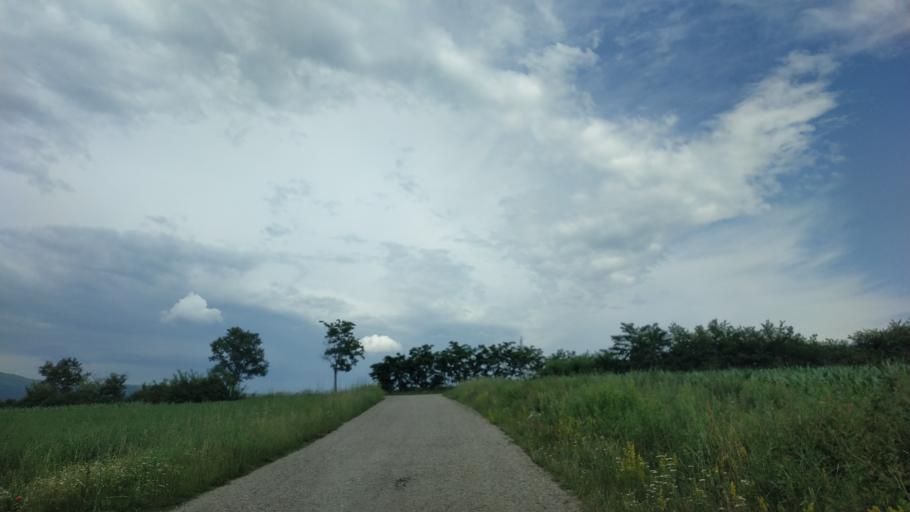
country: RS
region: Central Serbia
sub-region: Nisavski Okrug
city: Aleksinac
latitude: 43.6107
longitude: 21.6499
